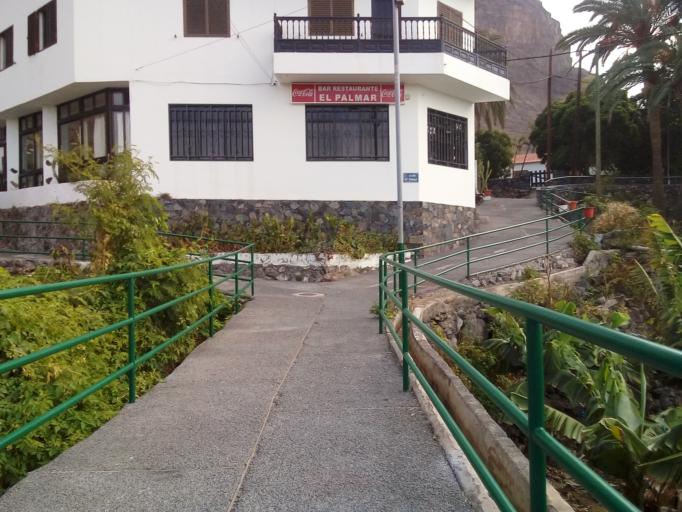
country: ES
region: Canary Islands
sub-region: Provincia de Santa Cruz de Tenerife
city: Alajero
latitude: 28.0903
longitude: -17.3357
